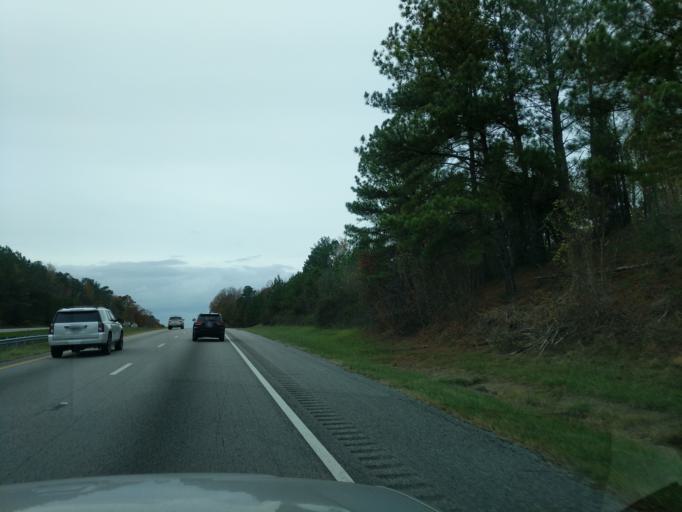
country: US
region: South Carolina
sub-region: Laurens County
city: Clinton
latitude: 34.4793
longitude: -81.8205
